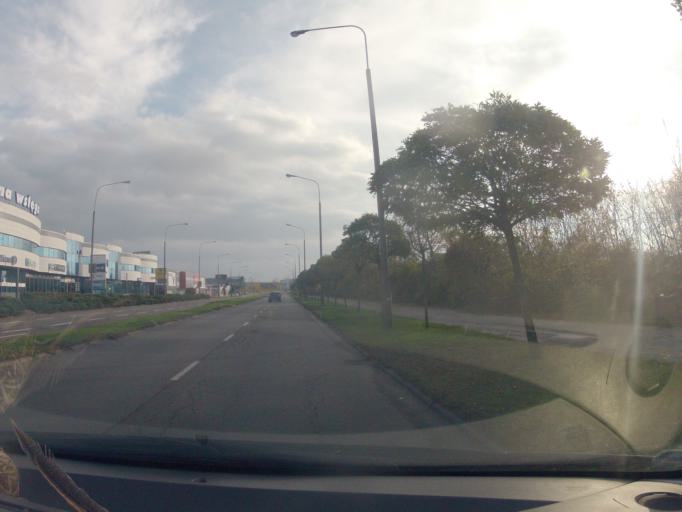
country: PL
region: Opole Voivodeship
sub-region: Powiat opolski
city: Opole
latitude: 50.6719
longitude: 17.9503
